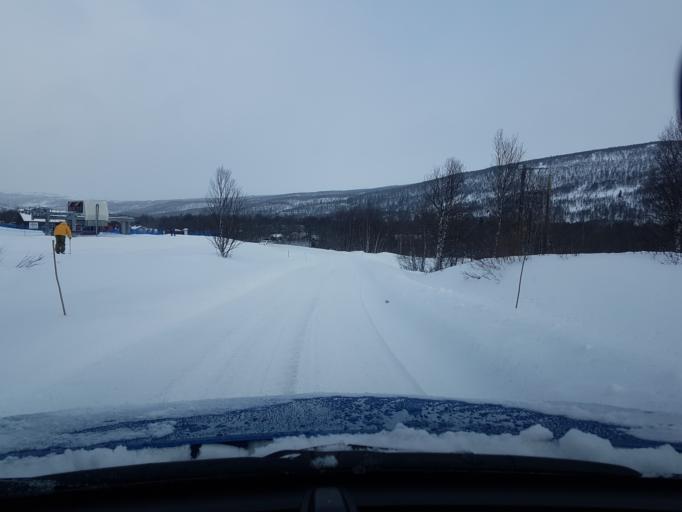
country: NO
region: Sor-Trondelag
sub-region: Tydal
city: Aas
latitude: 62.6938
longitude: 12.3983
